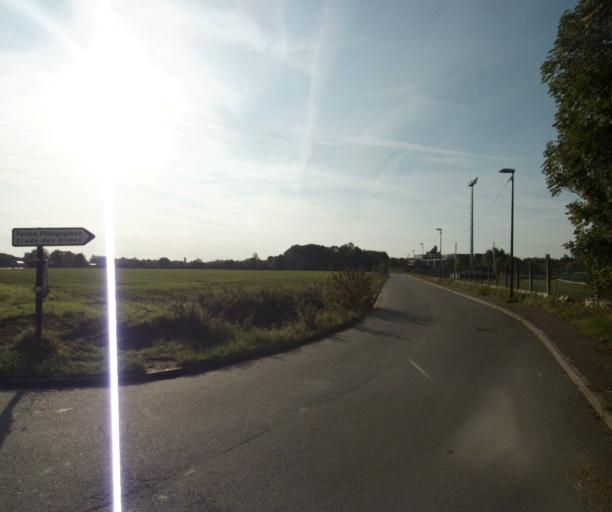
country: FR
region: Nord-Pas-de-Calais
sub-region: Departement du Nord
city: Lompret
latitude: 50.6577
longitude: 2.9920
